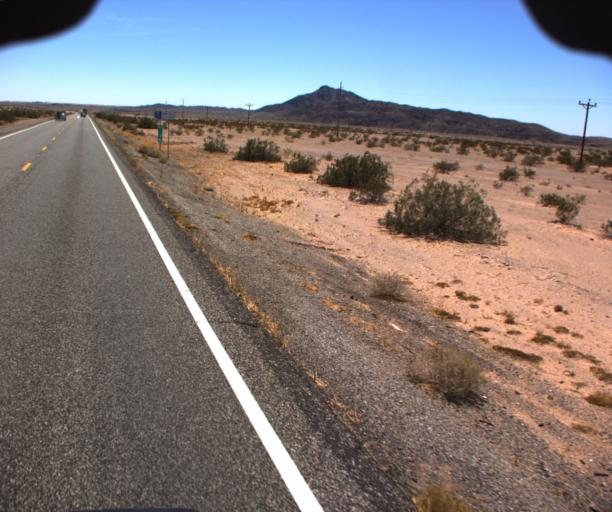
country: US
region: Arizona
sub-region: La Paz County
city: Parker
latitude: 34.0424
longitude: -114.2583
